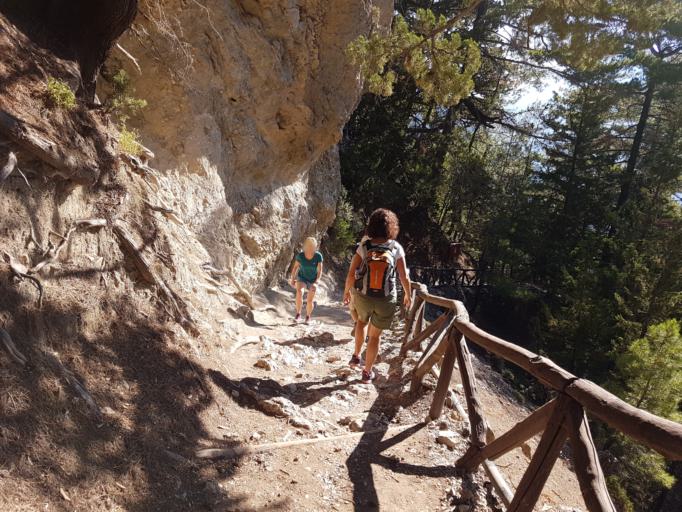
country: GR
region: Crete
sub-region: Nomos Chanias
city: Perivolia
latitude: 35.3076
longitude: 23.9212
